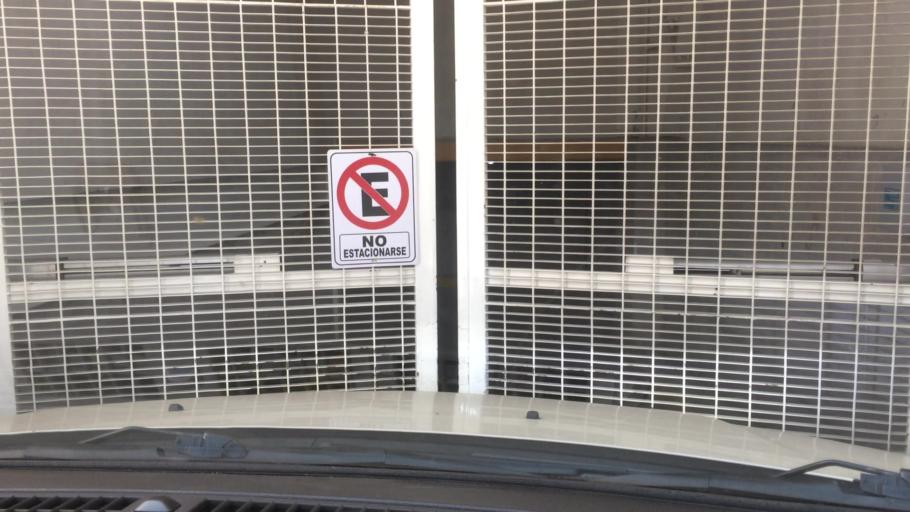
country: MX
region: Mexico City
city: Colonia del Valle
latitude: 19.3950
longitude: -99.1735
